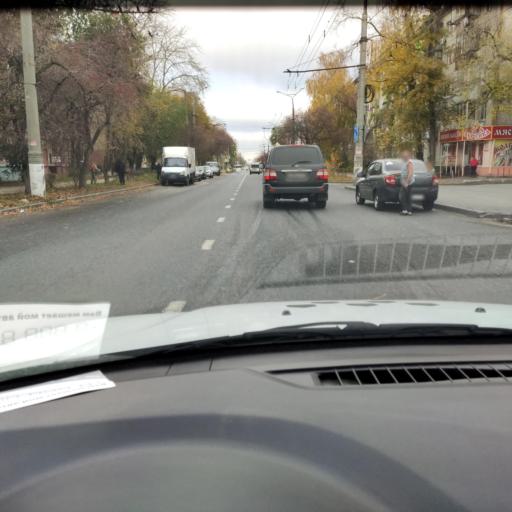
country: RU
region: Samara
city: Tol'yatti
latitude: 53.5149
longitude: 49.4173
